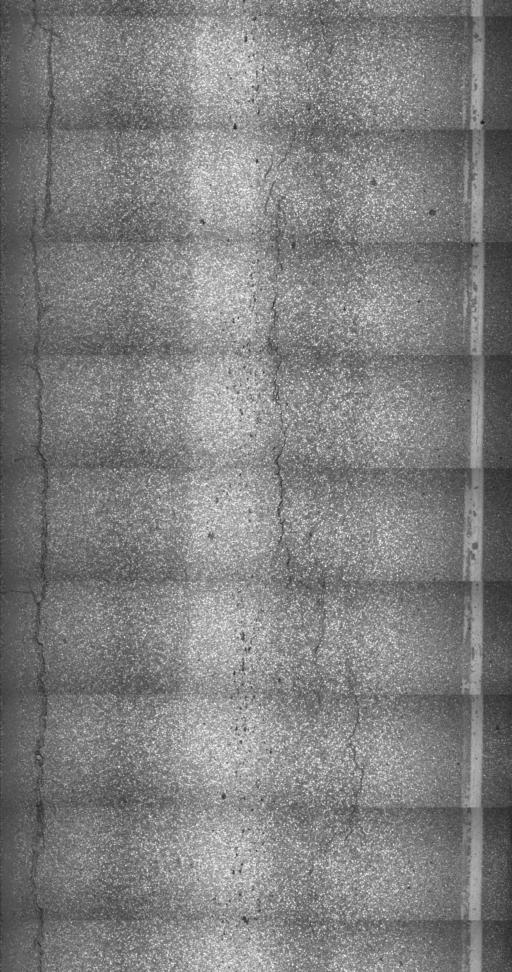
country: US
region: Vermont
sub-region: Franklin County
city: Saint Albans
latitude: 44.8011
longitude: -72.9500
